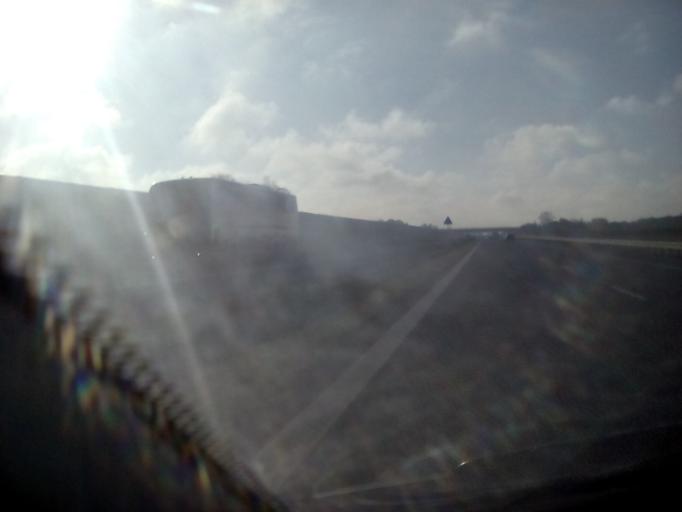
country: PL
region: Masovian Voivodeship
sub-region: Powiat grojecki
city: Jasieniec
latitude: 51.8035
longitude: 20.8880
